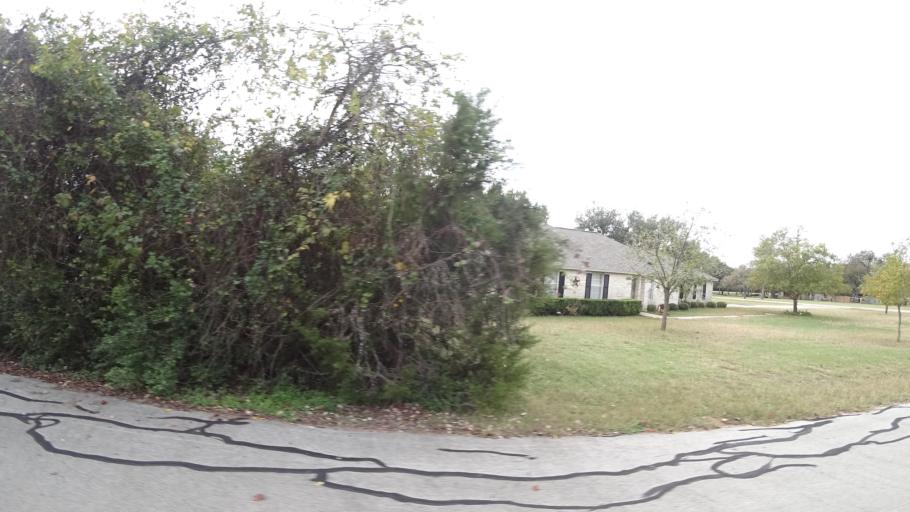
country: US
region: Texas
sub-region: Travis County
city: Shady Hollow
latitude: 30.1361
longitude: -97.8974
